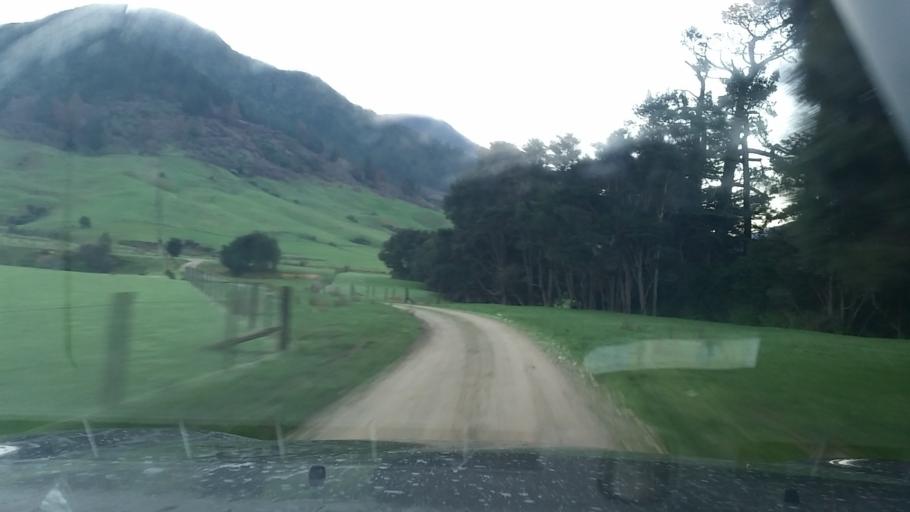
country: NZ
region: Marlborough
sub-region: Marlborough District
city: Picton
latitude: -41.1570
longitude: 174.1313
